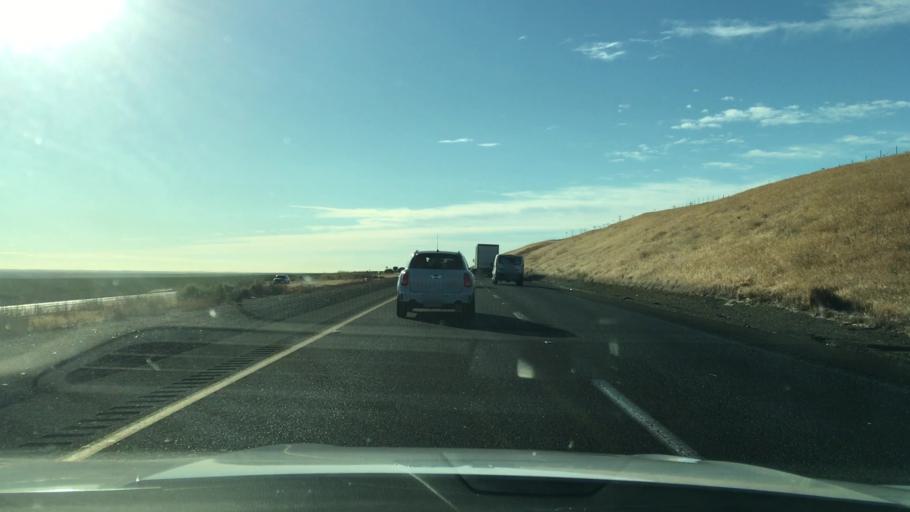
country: US
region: California
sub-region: Merced County
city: Los Banos
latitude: 36.9414
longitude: -120.8547
